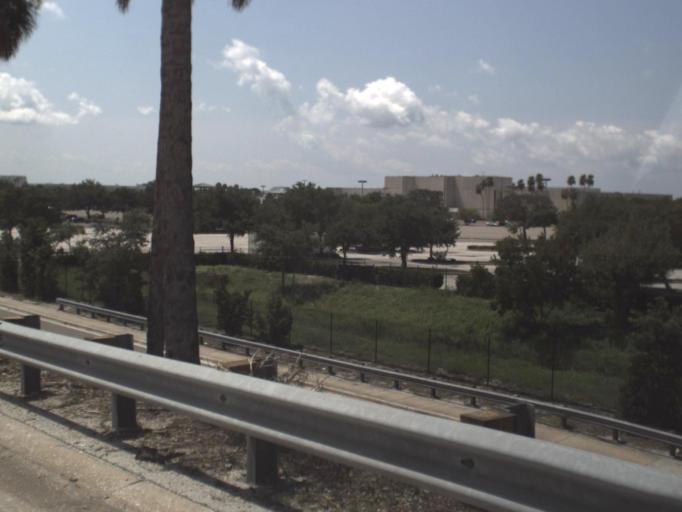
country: US
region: Florida
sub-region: Pinellas County
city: Kenneth City
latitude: 27.7985
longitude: -82.7364
